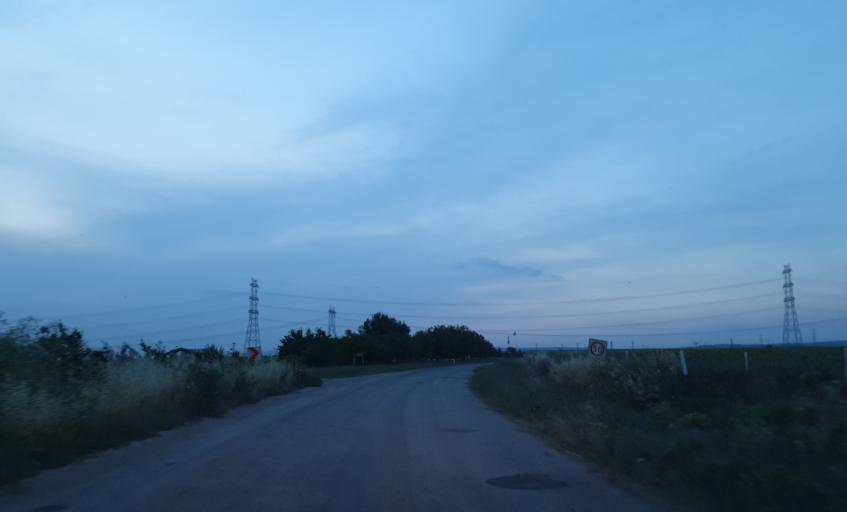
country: TR
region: Kirklareli
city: Vize
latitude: 41.4911
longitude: 27.7518
